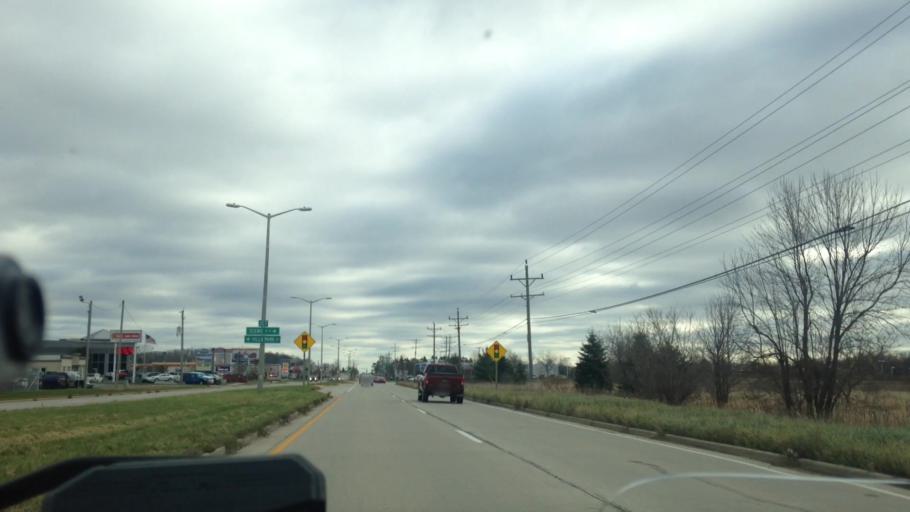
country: US
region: Wisconsin
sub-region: Washington County
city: West Bend
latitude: 43.4273
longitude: -88.2298
